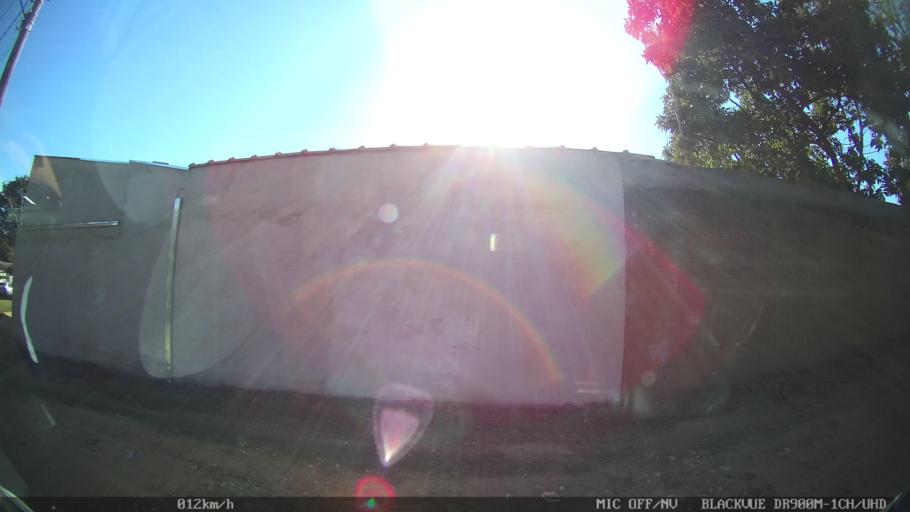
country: BR
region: Sao Paulo
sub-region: Franca
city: Franca
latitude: -20.4813
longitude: -47.4208
